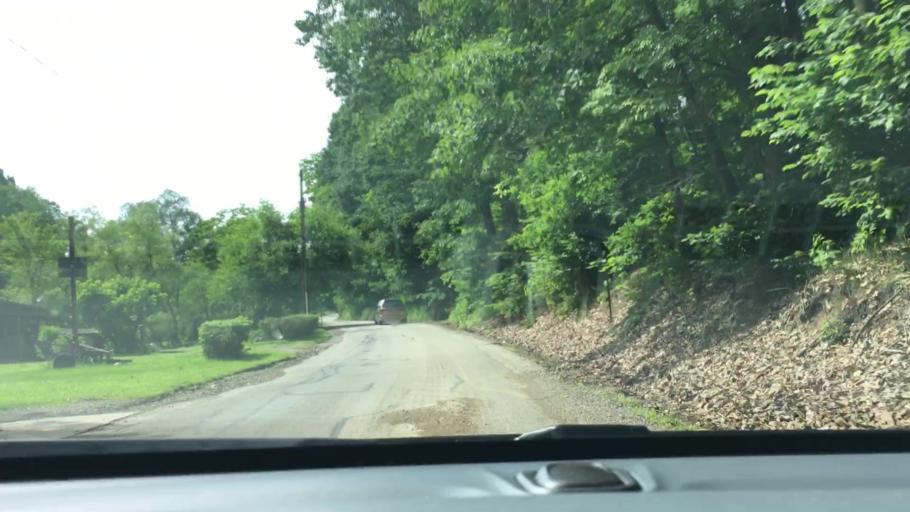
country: US
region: Pennsylvania
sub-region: Westmoreland County
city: Youngwood
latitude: 40.2539
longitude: -79.6085
